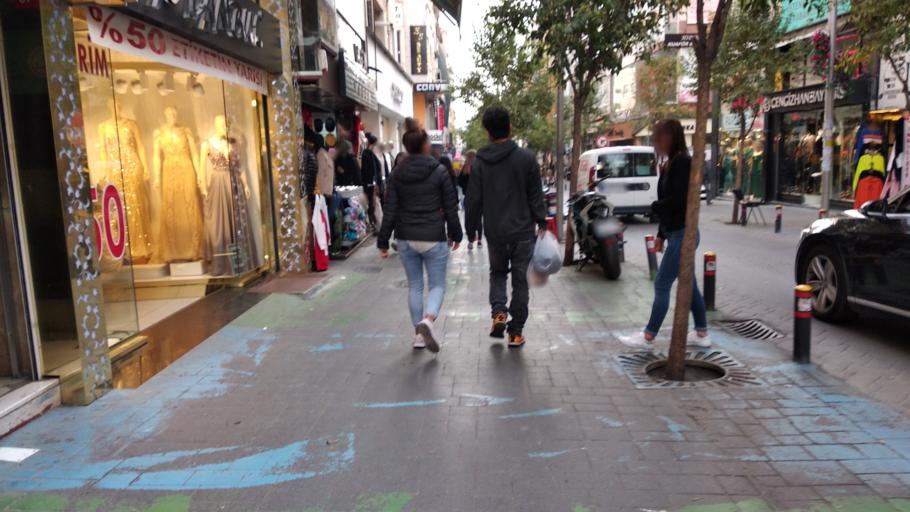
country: TR
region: Istanbul
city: Bahcelievler
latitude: 40.9763
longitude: 28.8750
